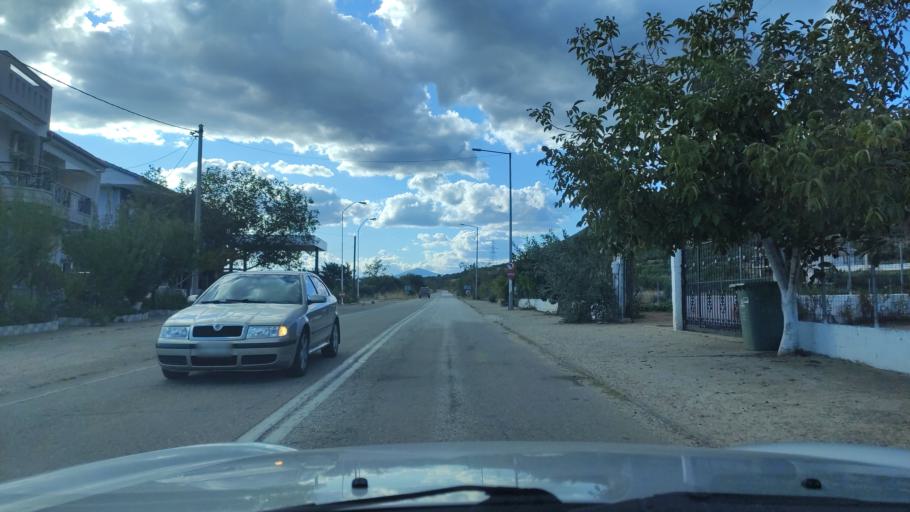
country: GR
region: East Macedonia and Thrace
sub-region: Nomos Rodopis
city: Iasmos
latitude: 41.1177
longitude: 25.1197
